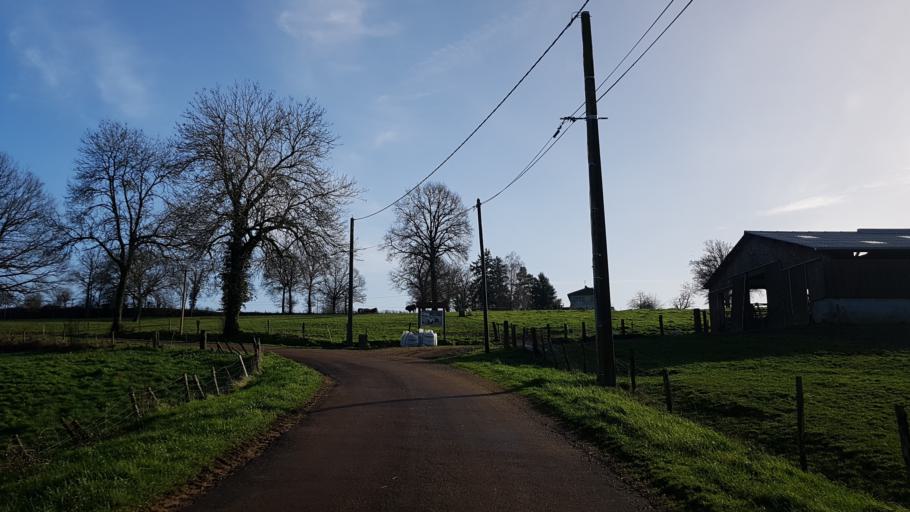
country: FR
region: Poitou-Charentes
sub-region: Departement de la Charente
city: Etagnac
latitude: 45.9297
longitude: 0.8018
